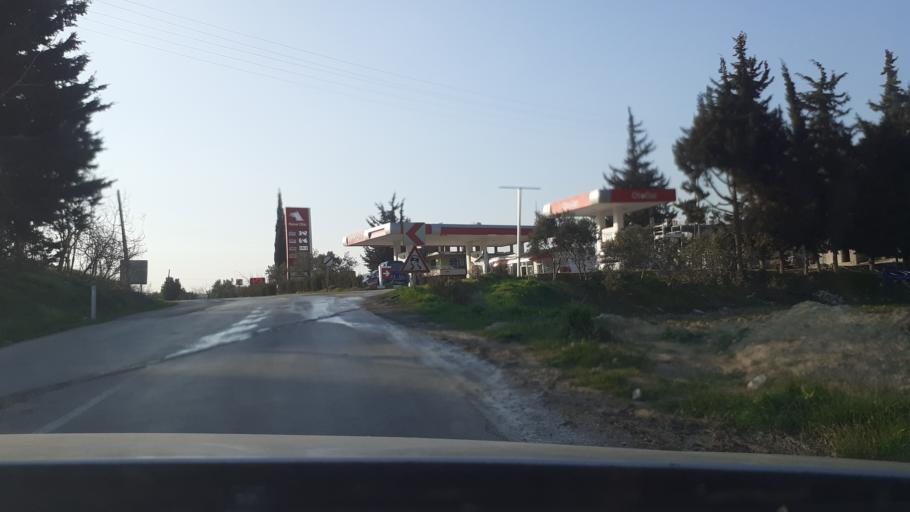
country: TR
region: Hatay
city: Fatikli
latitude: 36.1108
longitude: 36.2690
